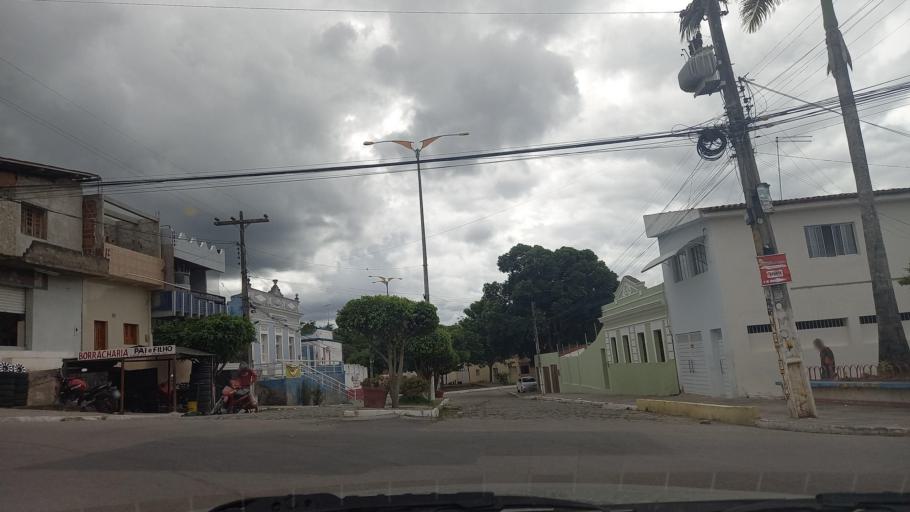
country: BR
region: Pernambuco
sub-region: Caruaru
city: Caruaru
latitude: -8.3254
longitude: -36.1378
